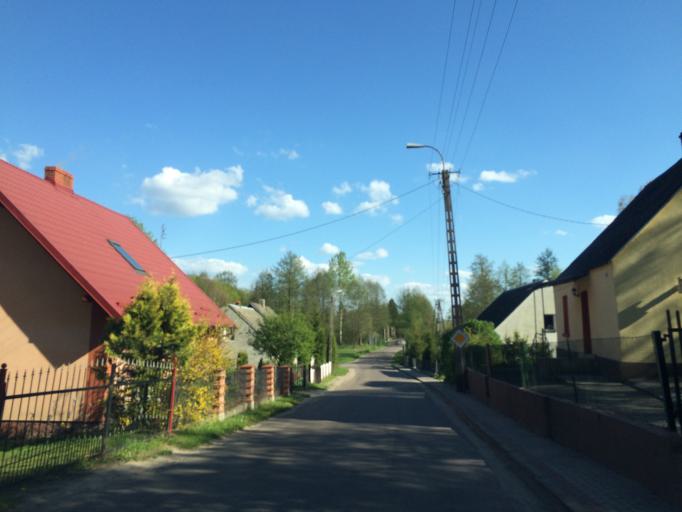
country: PL
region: Warmian-Masurian Voivodeship
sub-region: Powiat dzialdowski
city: Rybno
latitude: 53.4164
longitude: 19.9346
